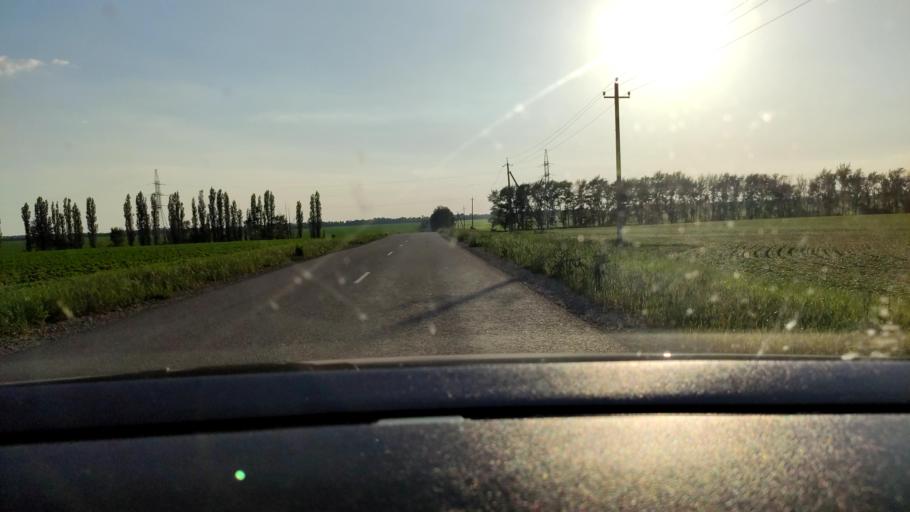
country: RU
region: Voronezj
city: Podkletnoye
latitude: 51.5064
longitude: 39.3971
